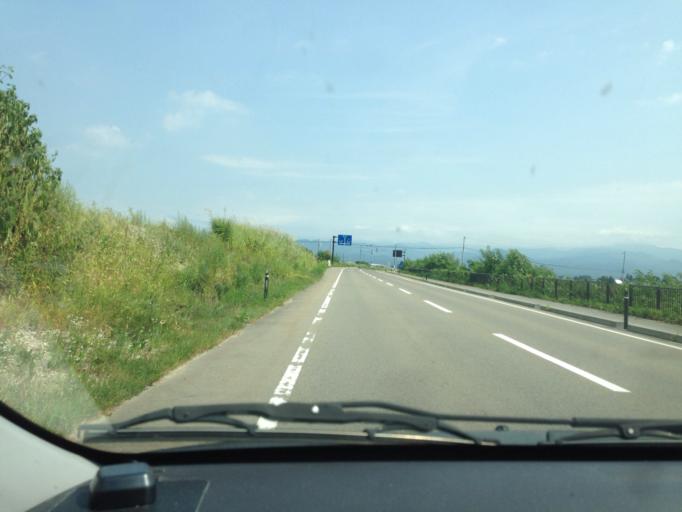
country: JP
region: Fukushima
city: Kitakata
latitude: 37.6094
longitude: 139.8498
